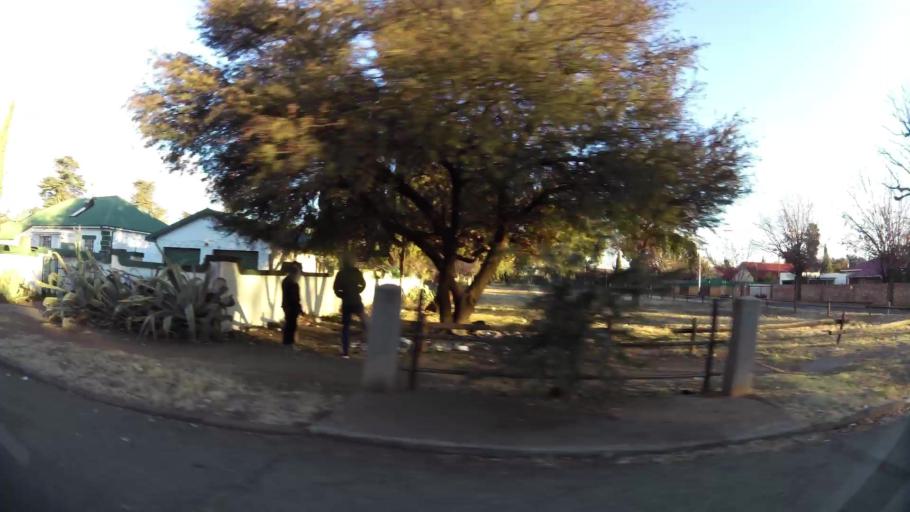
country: ZA
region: North-West
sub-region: Dr Kenneth Kaunda District Municipality
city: Potchefstroom
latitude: -26.7205
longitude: 27.0897
